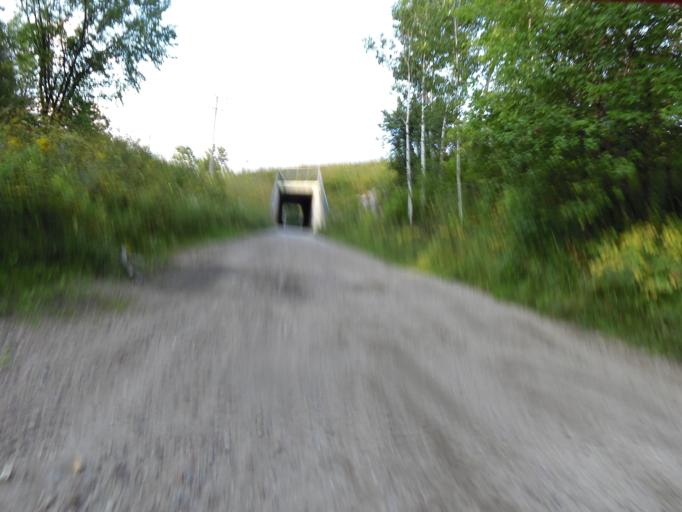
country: CA
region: Quebec
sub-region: Outaouais
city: Maniwaki
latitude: 46.3657
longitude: -75.9837
